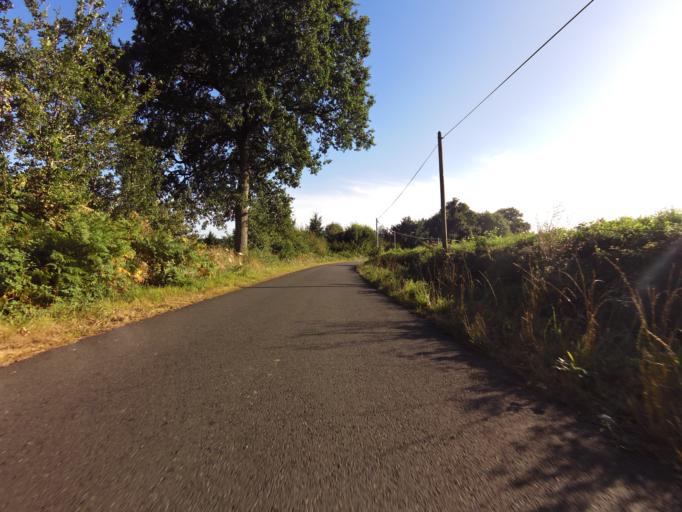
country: FR
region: Brittany
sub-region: Departement du Morbihan
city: Pluherlin
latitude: 47.7193
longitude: -2.3548
